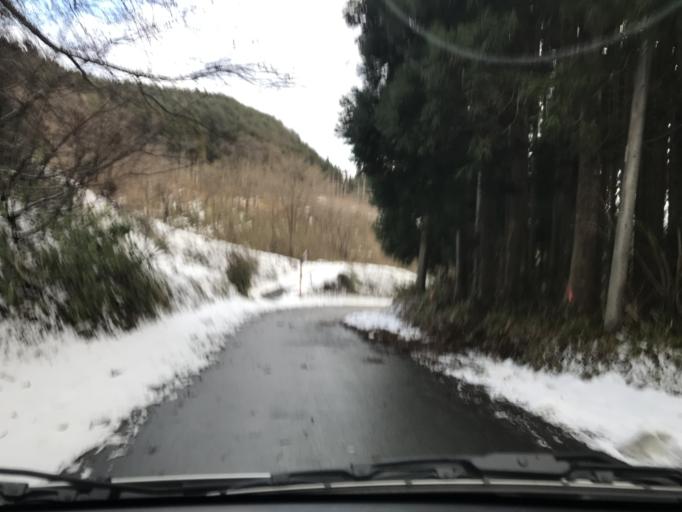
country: JP
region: Iwate
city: Ichinoseki
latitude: 39.0120
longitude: 140.9778
